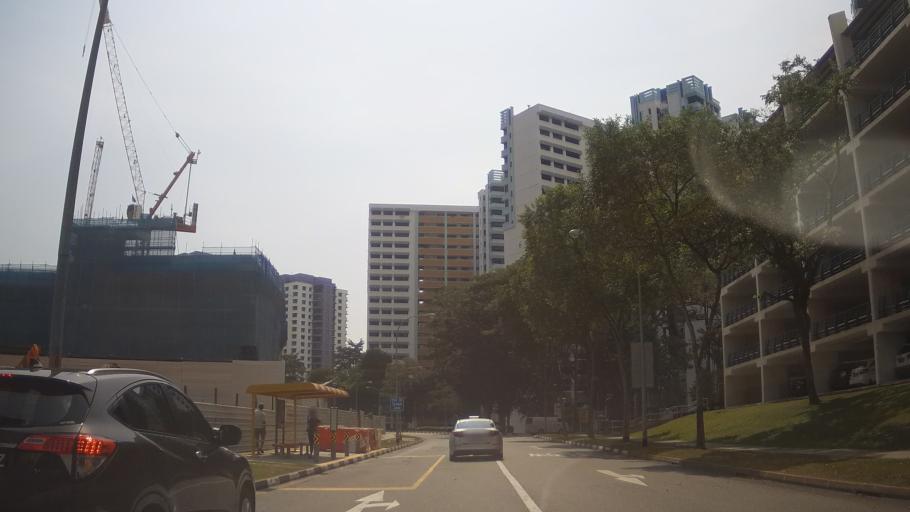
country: MY
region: Johor
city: Johor Bahru
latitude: 1.3869
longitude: 103.7606
